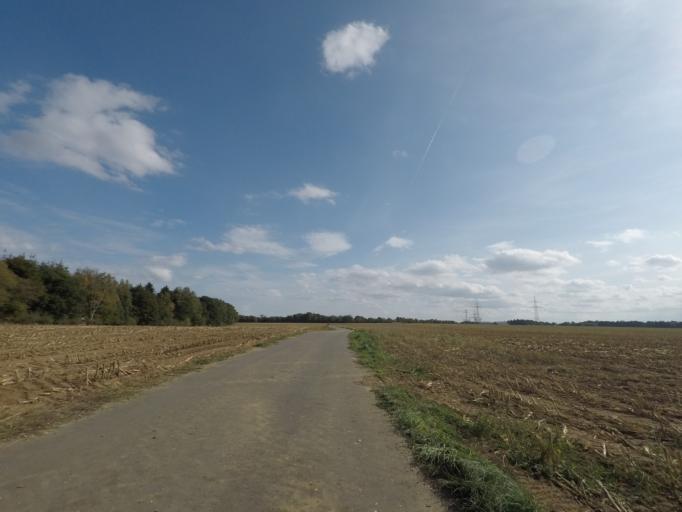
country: LU
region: Luxembourg
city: Itzig
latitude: 49.6044
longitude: 6.1780
